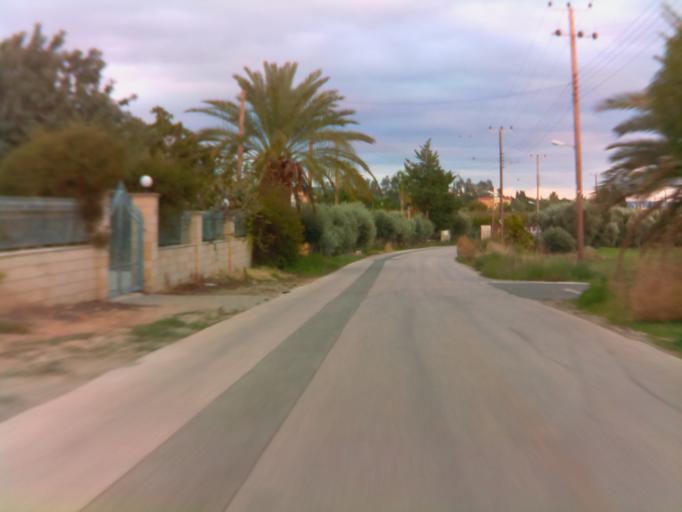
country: CY
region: Pafos
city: Pegeia
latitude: 34.8692
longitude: 32.3489
